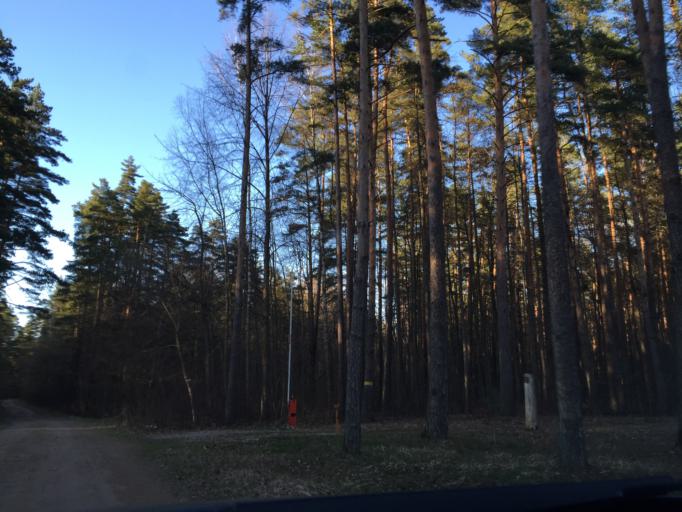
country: LV
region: Kekava
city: Kekava
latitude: 56.8549
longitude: 24.2321
